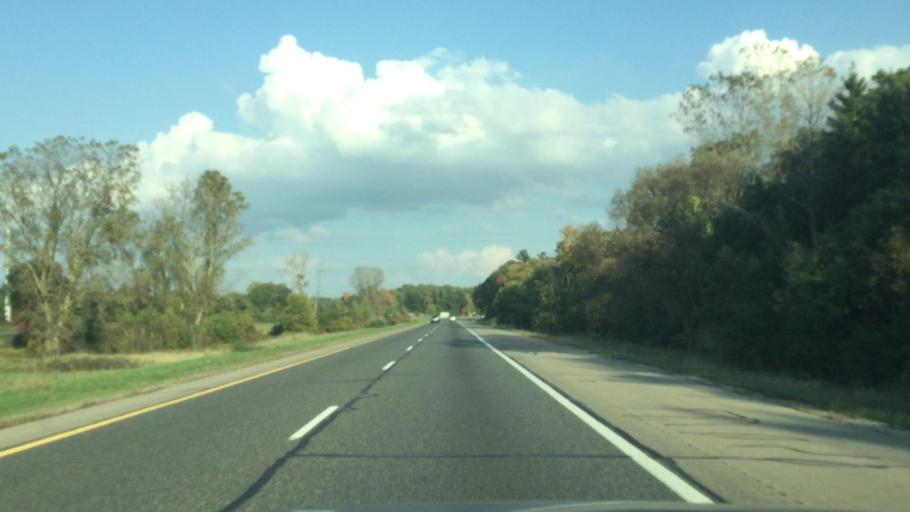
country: US
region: Michigan
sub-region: Washtenaw County
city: Chelsea
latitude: 42.2990
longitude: -83.9531
